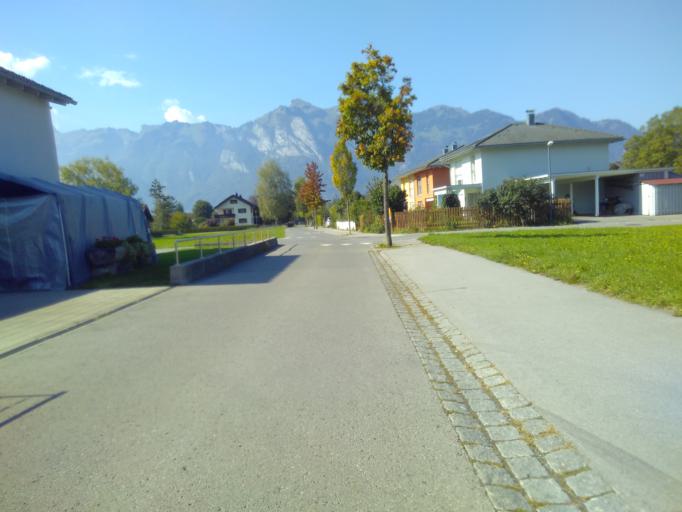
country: AT
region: Vorarlberg
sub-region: Politischer Bezirk Feldkirch
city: Nofels
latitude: 47.2587
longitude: 9.5706
